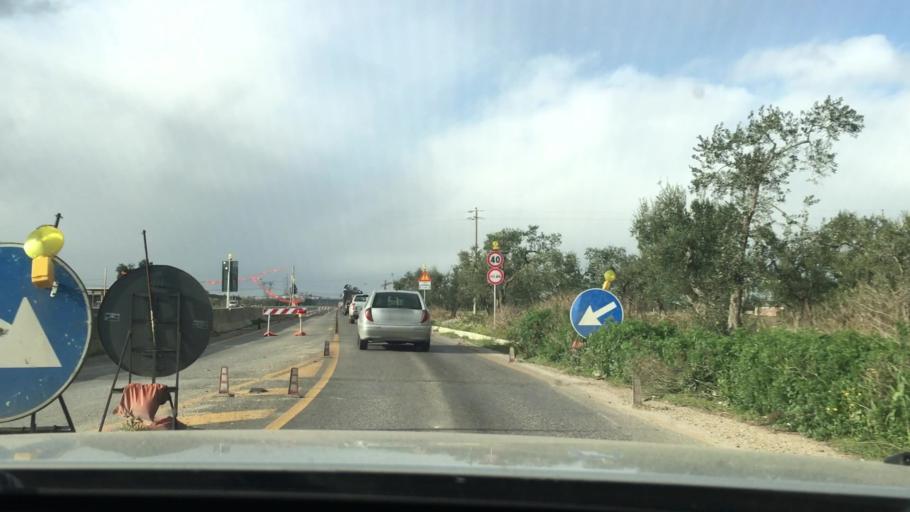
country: IT
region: Apulia
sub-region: Provincia di Bari
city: Bitetto
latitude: 41.0733
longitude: 16.7486
